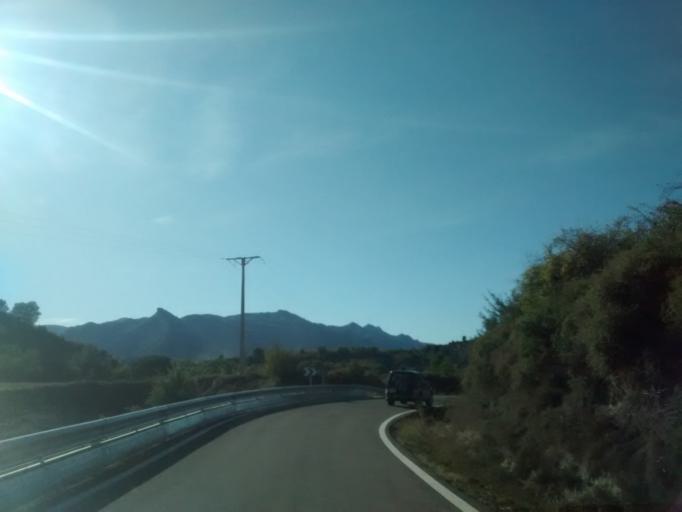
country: ES
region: Aragon
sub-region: Provincia de Huesca
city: Loarre
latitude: 42.3880
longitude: -0.7086
